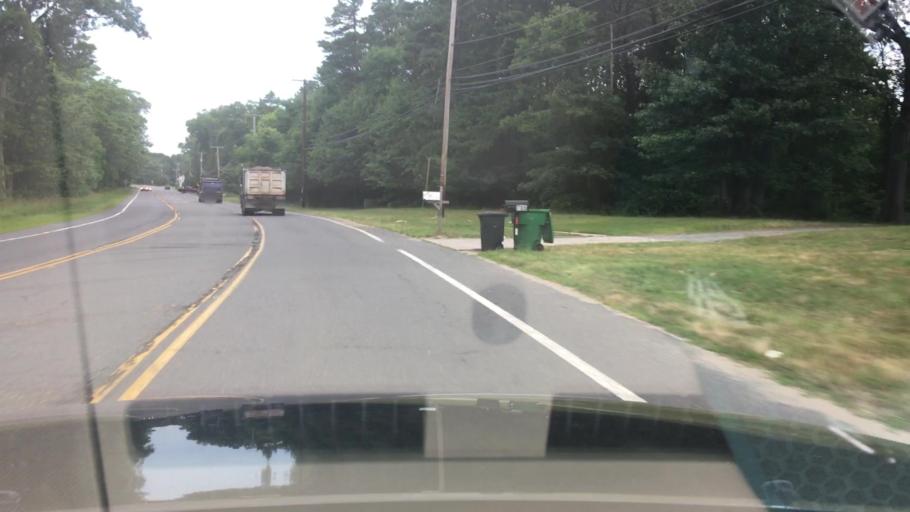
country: US
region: New Jersey
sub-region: Ocean County
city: Lakehurst
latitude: 40.0675
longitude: -74.3646
